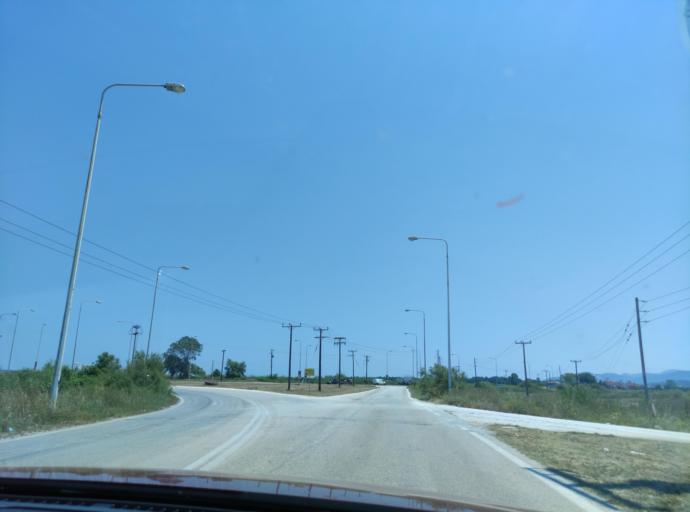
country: GR
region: East Macedonia and Thrace
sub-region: Nomos Kavalas
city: Keramoti
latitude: 40.8693
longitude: 24.7039
